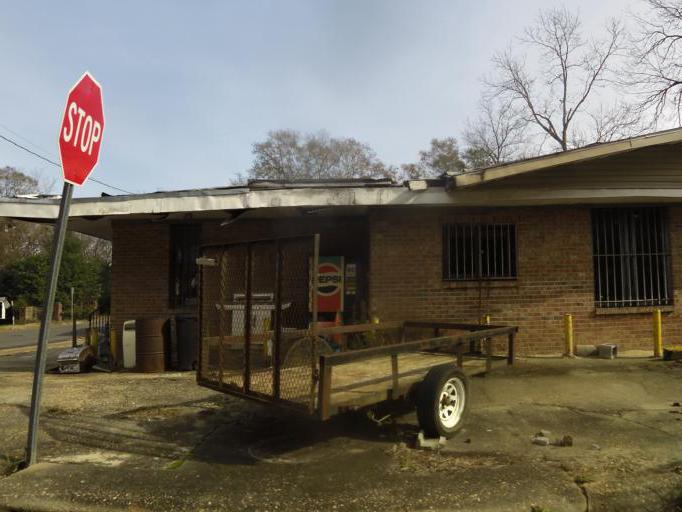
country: US
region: Alabama
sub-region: Houston County
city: Dothan
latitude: 31.2264
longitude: -85.3817
